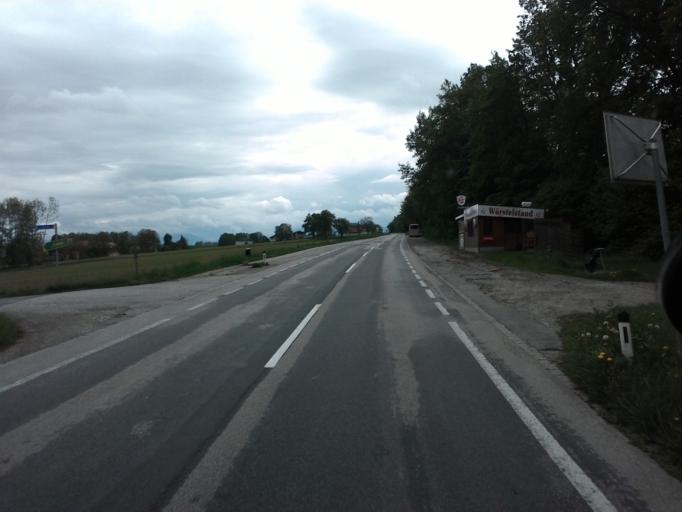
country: AT
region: Upper Austria
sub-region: Wels-Land
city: Sattledt
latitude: 48.0209
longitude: 14.0604
